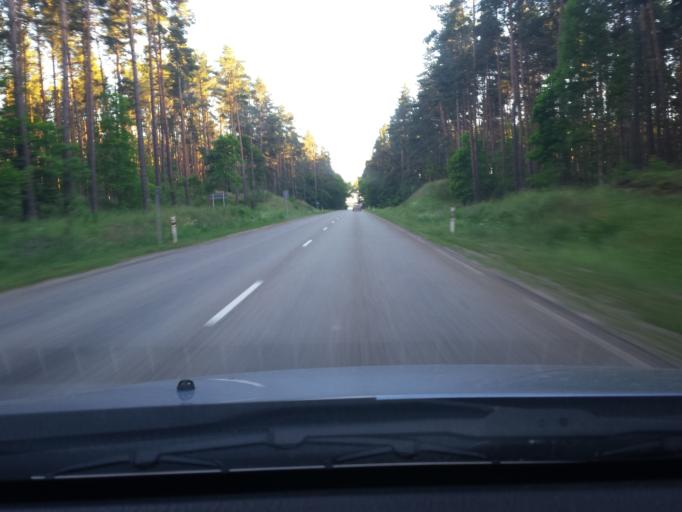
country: LV
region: Riga
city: Jaunciems
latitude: 57.0572
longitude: 24.1559
